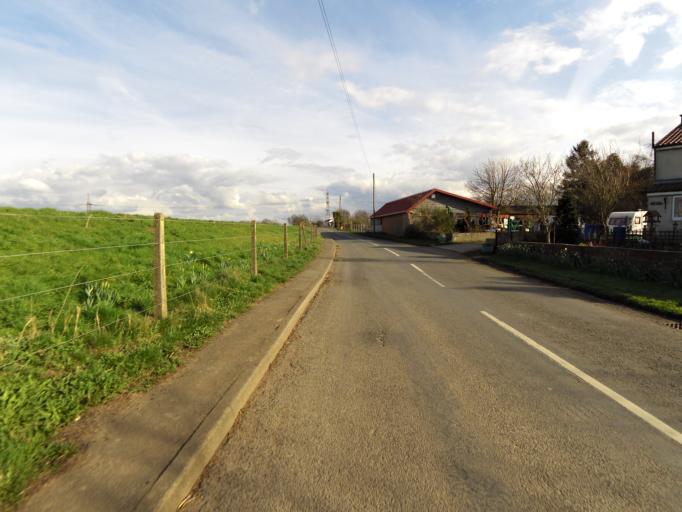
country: GB
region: England
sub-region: East Riding of Yorkshire
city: Snaith
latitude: 53.6925
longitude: -1.0511
